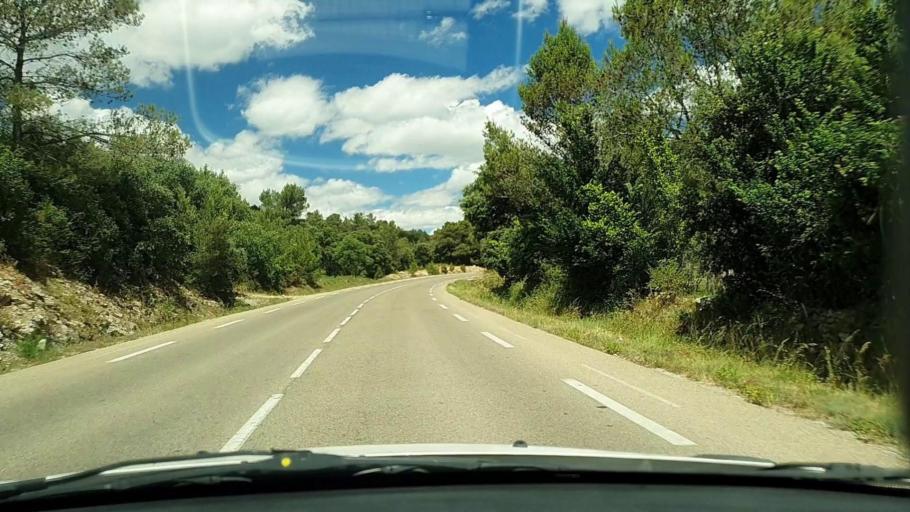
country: FR
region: Languedoc-Roussillon
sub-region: Departement du Gard
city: Poulx
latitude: 43.8830
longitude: 4.4169
